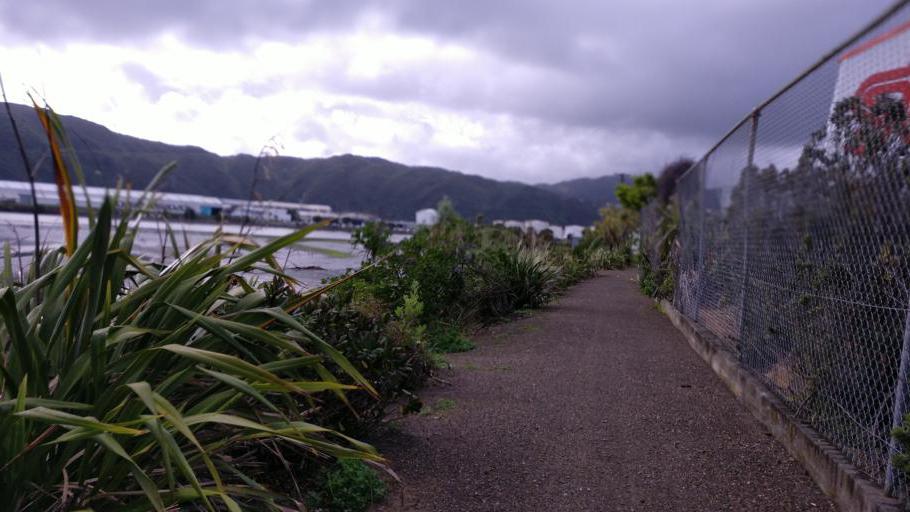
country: NZ
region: Wellington
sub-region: Lower Hutt City
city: Lower Hutt
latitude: -41.2334
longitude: 174.8971
